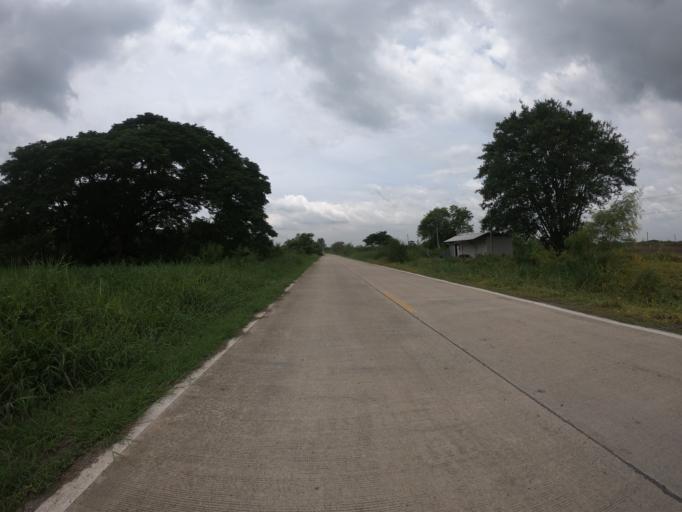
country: TH
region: Pathum Thani
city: Ban Lam Luk Ka
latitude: 13.9650
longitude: 100.8527
